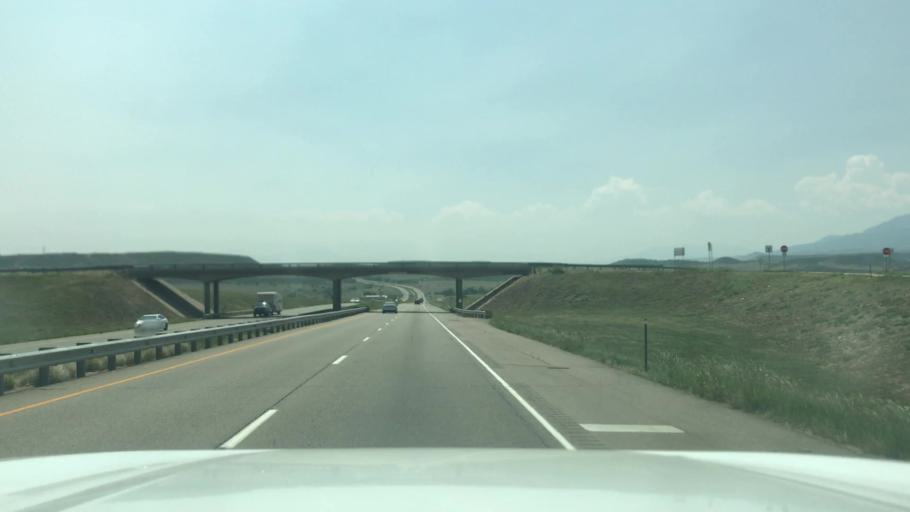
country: US
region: Colorado
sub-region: Pueblo County
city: Colorado City
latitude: 37.9263
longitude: -104.8218
